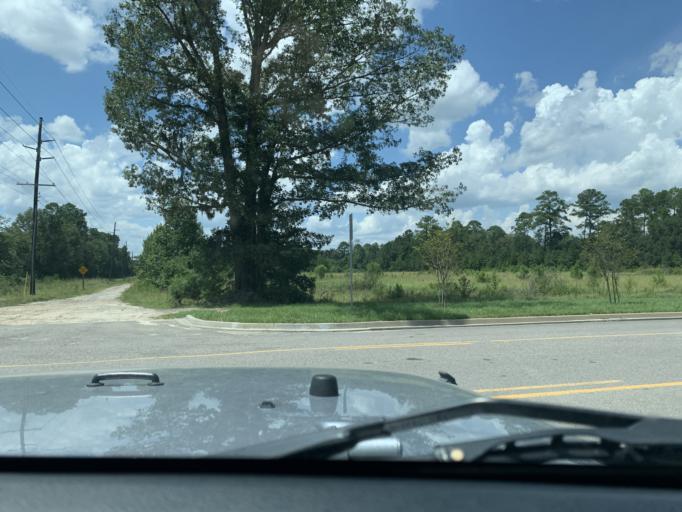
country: US
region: Georgia
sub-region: Chatham County
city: Bloomingdale
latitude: 32.1220
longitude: -81.2753
